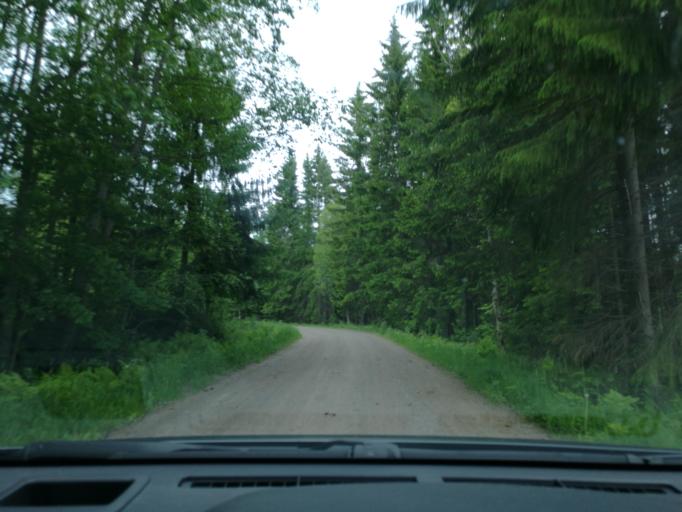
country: SE
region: Dalarna
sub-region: Smedjebackens Kommun
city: Smedjebacken
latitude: 60.1432
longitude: 15.3077
